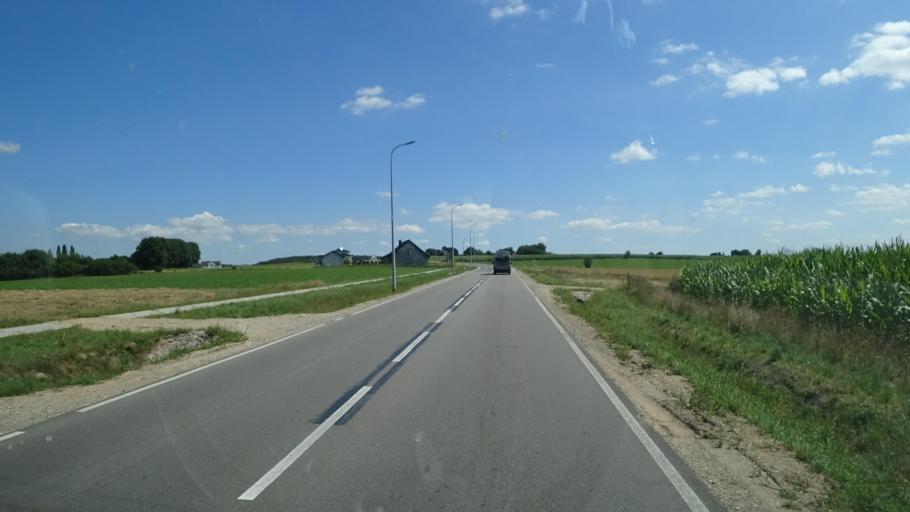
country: PL
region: Podlasie
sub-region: Powiat lomzynski
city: Piatnica
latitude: 53.2486
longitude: 22.1094
